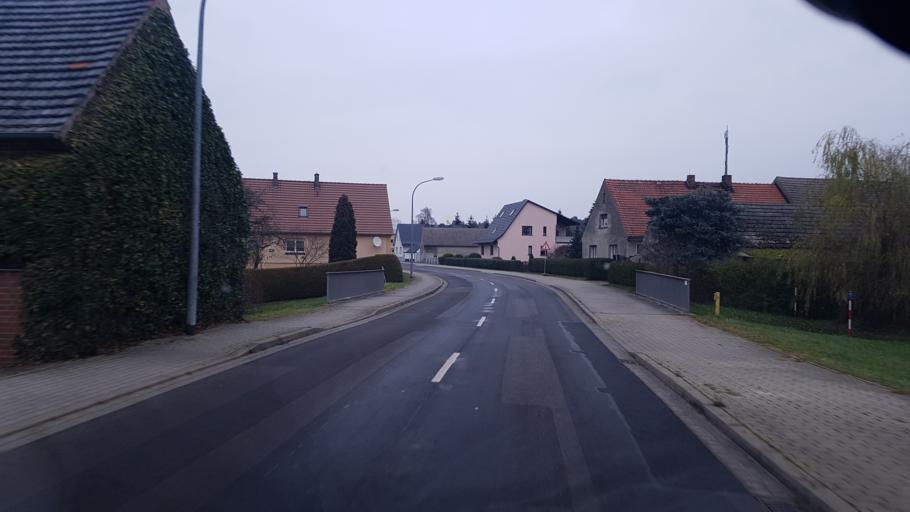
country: DE
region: Brandenburg
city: Schenkendobern
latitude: 51.9393
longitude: 14.5670
